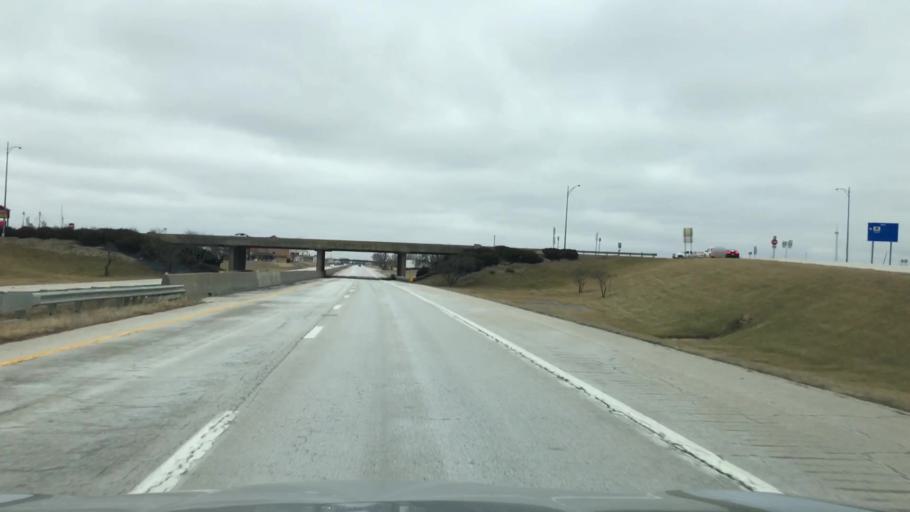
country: US
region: Missouri
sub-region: Livingston County
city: Chillicothe
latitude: 39.7731
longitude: -93.5542
